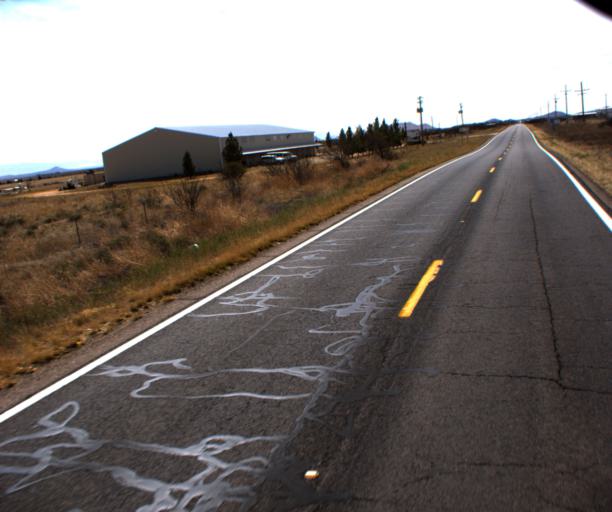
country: US
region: Arizona
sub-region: Cochise County
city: Willcox
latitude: 31.9879
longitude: -109.8549
